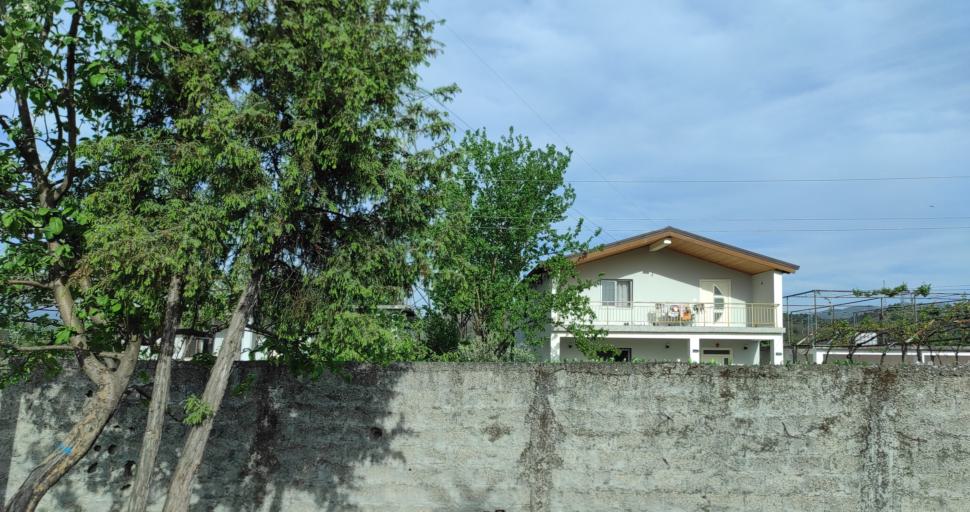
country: AL
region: Shkoder
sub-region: Rrethi i Shkodres
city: Shkoder
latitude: 42.0715
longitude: 19.5295
